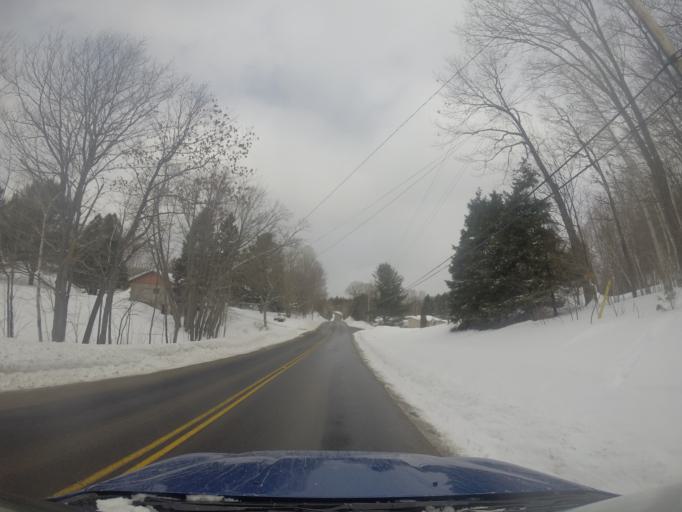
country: CA
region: Ontario
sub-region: Parry Sound District
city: Parry Sound
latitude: 45.3857
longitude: -80.0266
